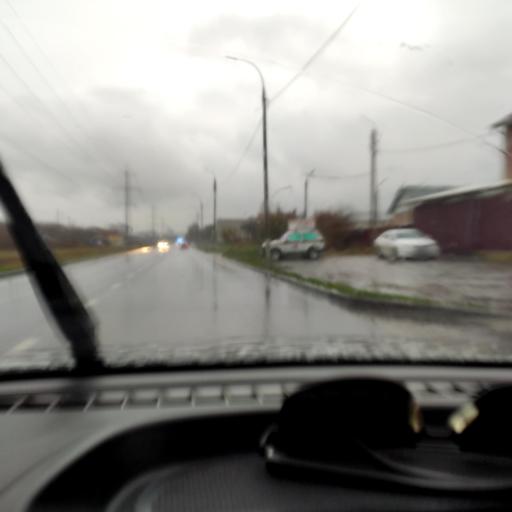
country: RU
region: Samara
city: Tol'yatti
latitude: 53.5185
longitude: 49.3957
